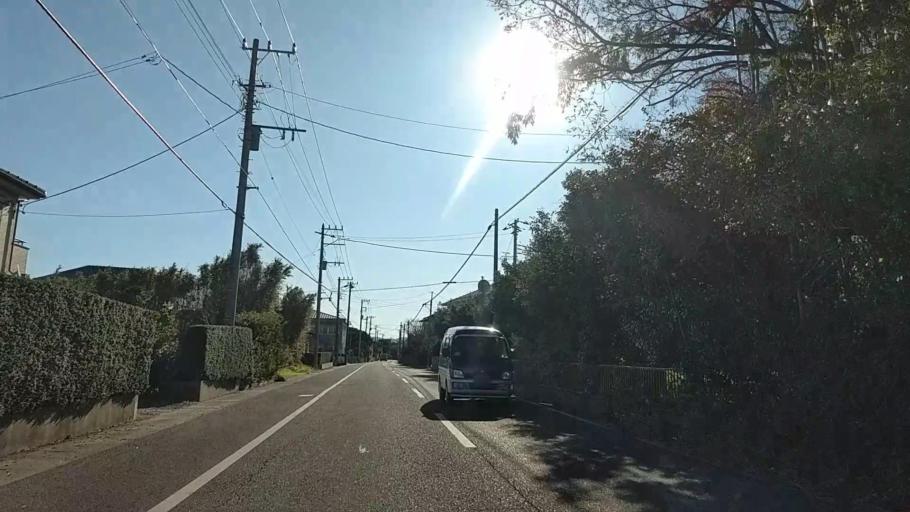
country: JP
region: Chiba
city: Futtsu
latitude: 35.3058
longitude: 139.8317
